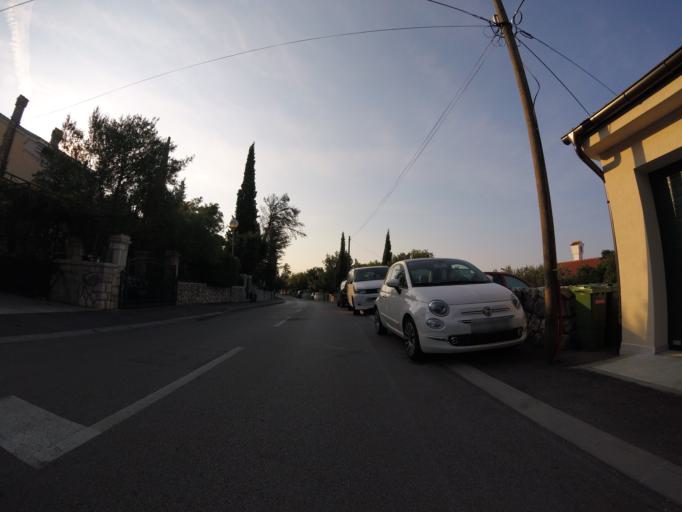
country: HR
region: Primorsko-Goranska
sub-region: Grad Crikvenica
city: Crikvenica
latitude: 45.1954
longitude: 14.6638
